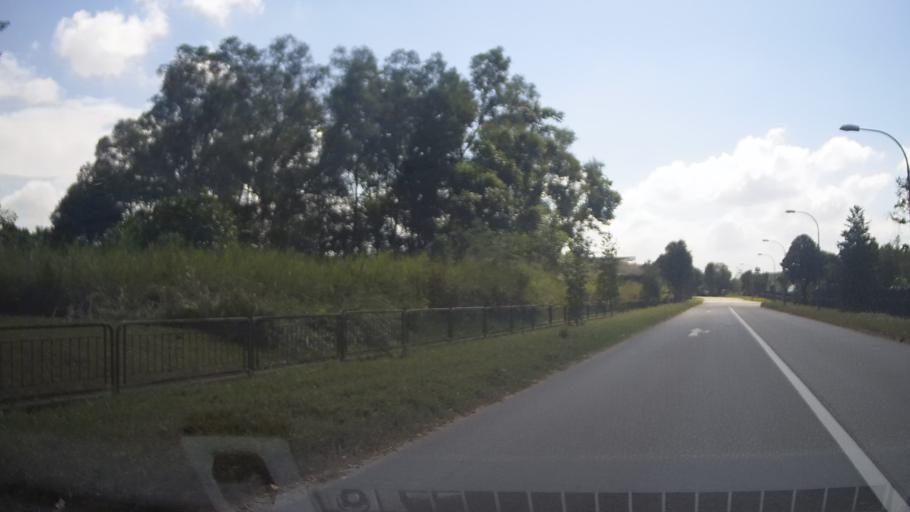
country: MY
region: Johor
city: Johor Bahru
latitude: 1.4329
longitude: 103.7158
